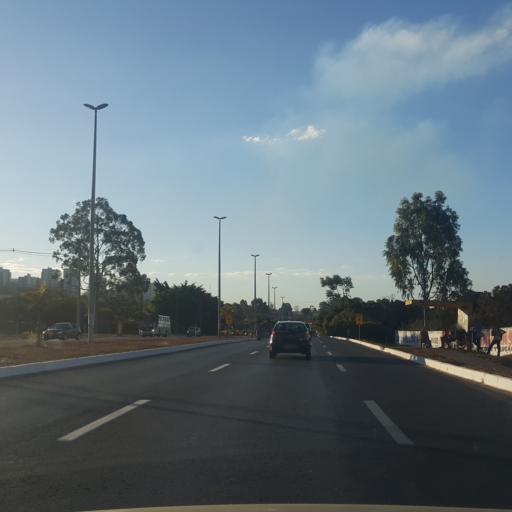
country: BR
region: Federal District
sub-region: Brasilia
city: Brasilia
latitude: -15.8438
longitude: -48.0009
